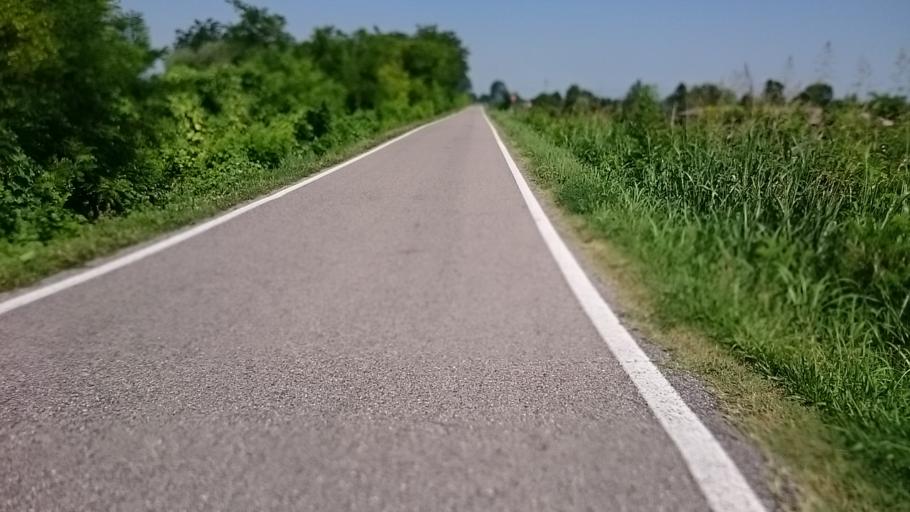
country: IT
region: Veneto
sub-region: Provincia di Venezia
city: Galta
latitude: 45.3772
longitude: 12.0249
